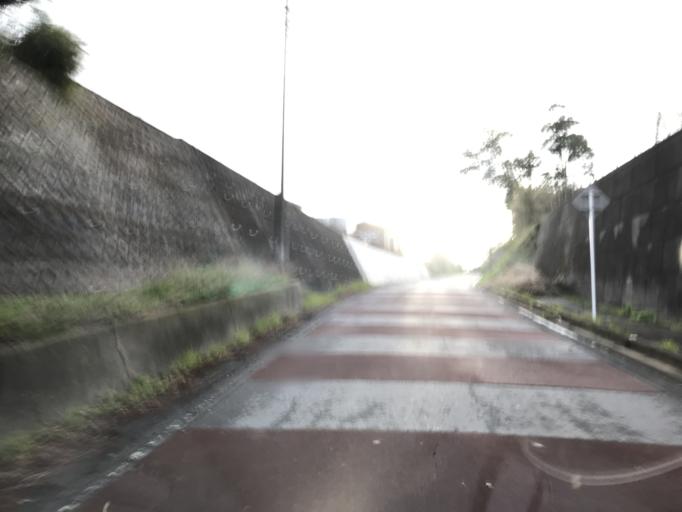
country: JP
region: Chiba
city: Yokaichiba
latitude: 35.7449
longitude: 140.5074
